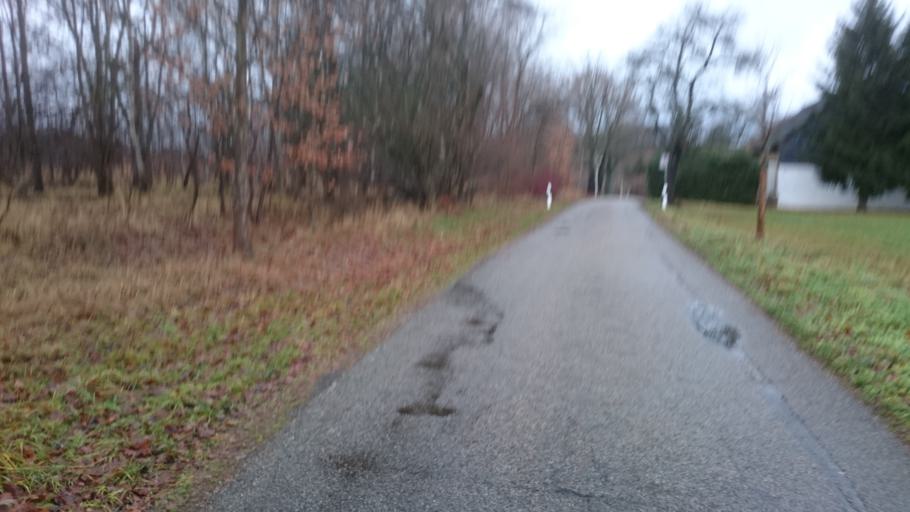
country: DE
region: Saxony
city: Mulsen
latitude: 50.7487
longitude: 12.5288
